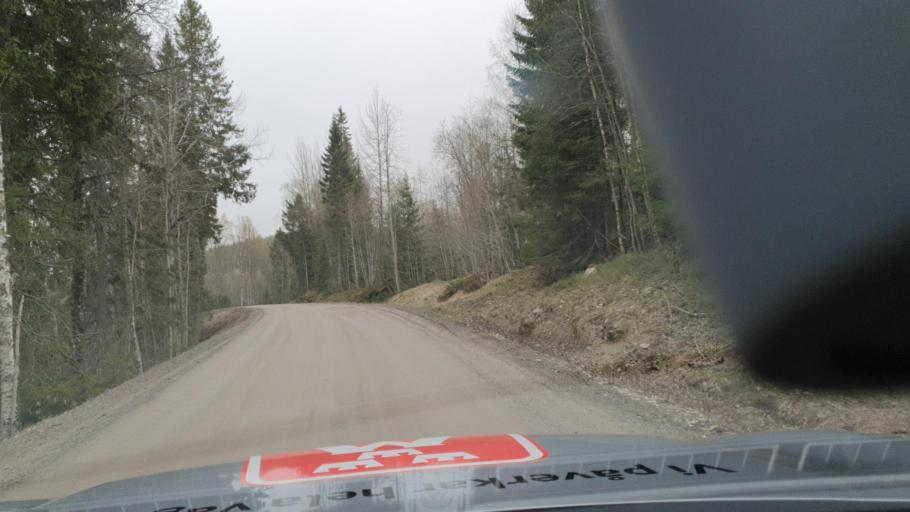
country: SE
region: Vaesternorrland
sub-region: OErnskoeldsviks Kommun
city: Husum
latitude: 63.6343
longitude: 19.0591
